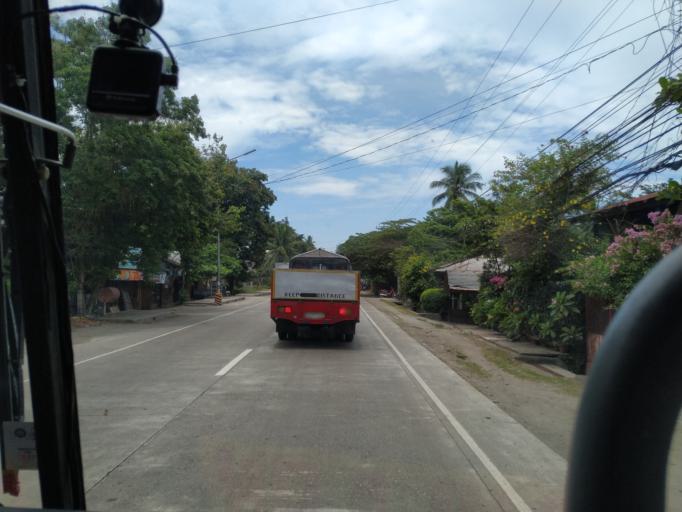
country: PH
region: Central Visayas
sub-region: Province of Negros Oriental
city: Sibulan
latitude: 9.3505
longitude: 123.2855
